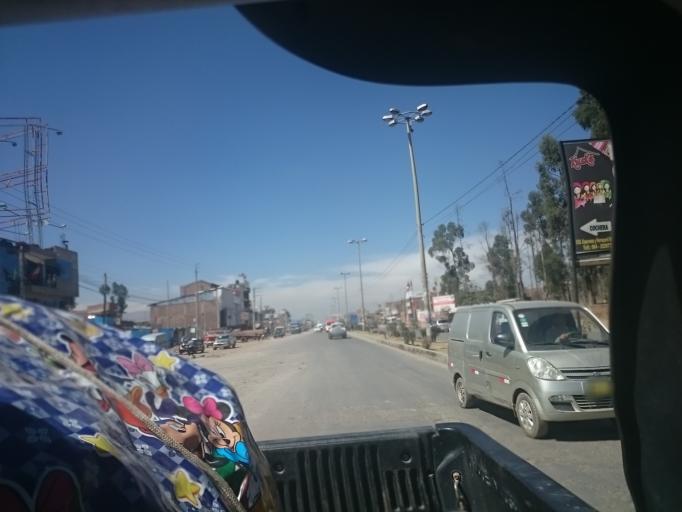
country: PE
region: Junin
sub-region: Provincia de Huancayo
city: Pilcomay
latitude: -12.0377
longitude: -75.2297
